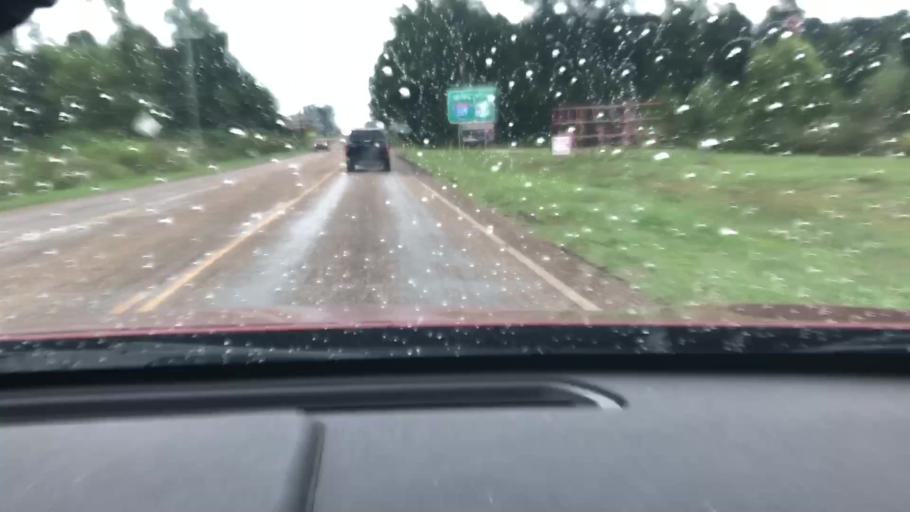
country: US
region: Texas
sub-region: Bowie County
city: Wake Village
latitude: 33.4436
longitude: -94.1059
